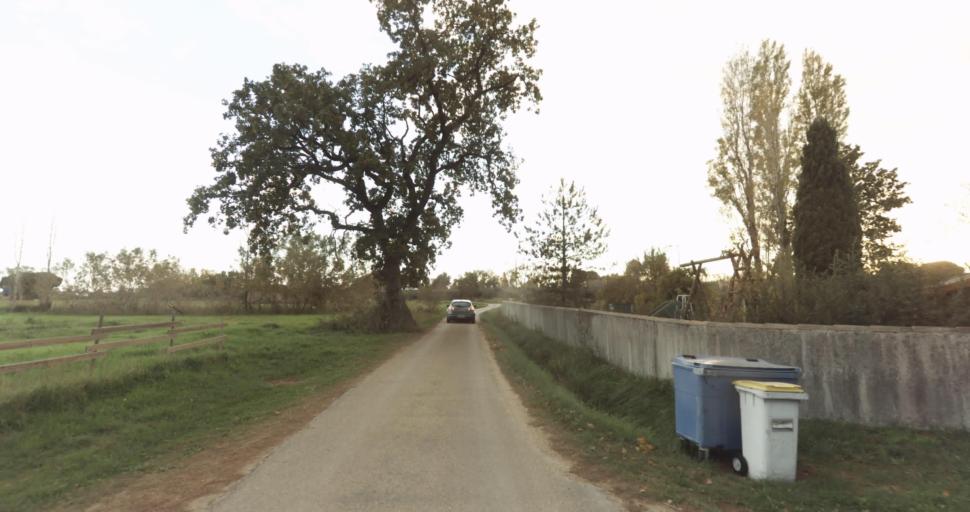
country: FR
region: Languedoc-Roussillon
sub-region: Departement du Gard
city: Aigues-Mortes
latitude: 43.5817
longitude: 4.2009
